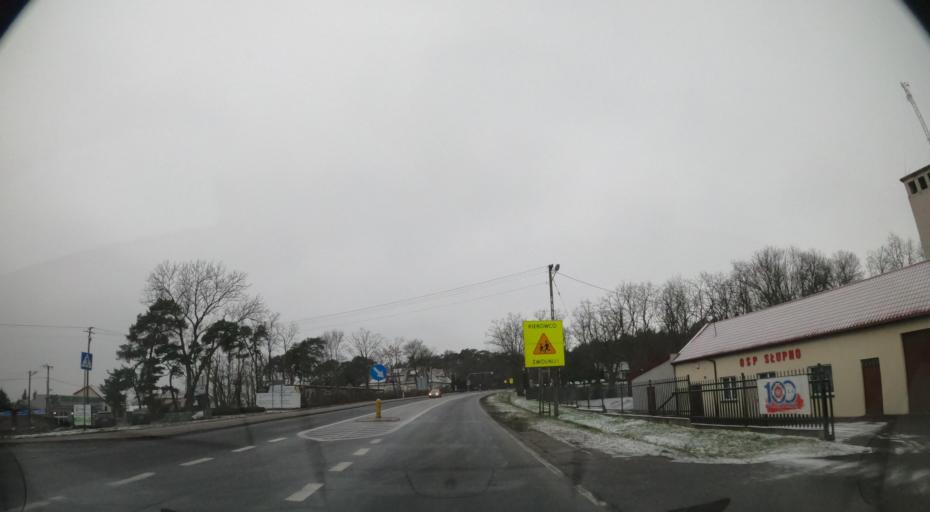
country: PL
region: Masovian Voivodeship
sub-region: Powiat plocki
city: Slupno
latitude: 52.4999
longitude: 19.8432
